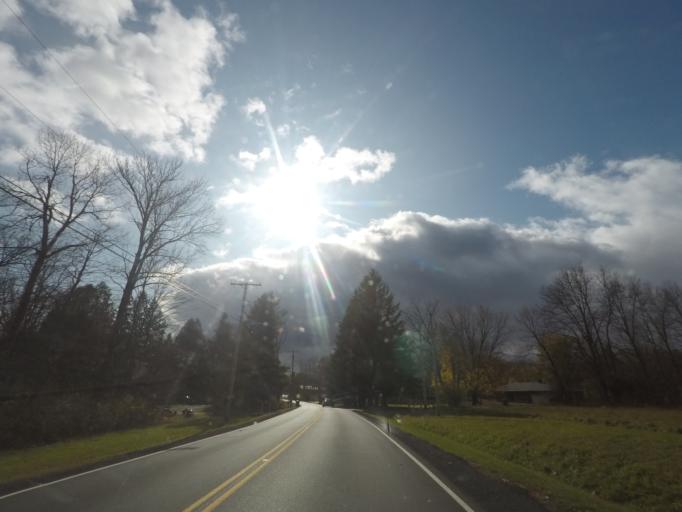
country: US
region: New York
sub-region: Saratoga County
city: Country Knolls
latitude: 42.9299
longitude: -73.8554
